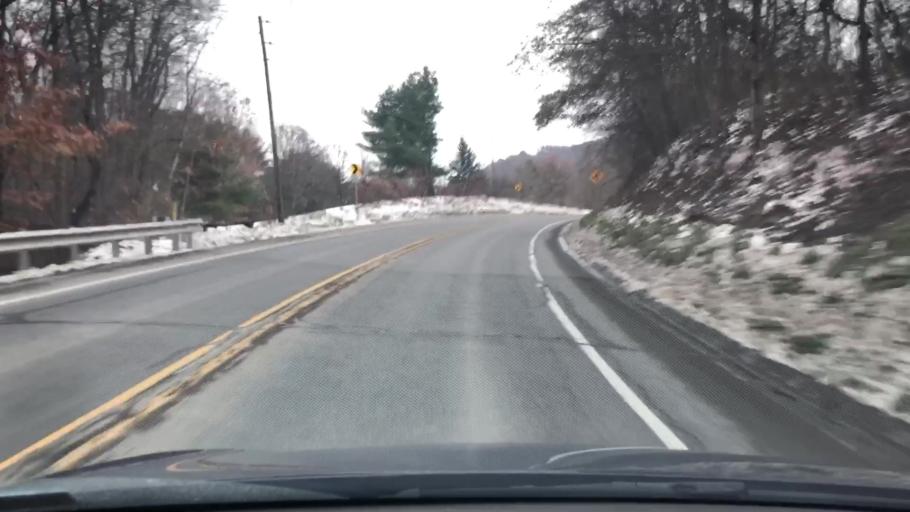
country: US
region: Pennsylvania
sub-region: Jefferson County
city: Brookville
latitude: 41.1283
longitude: -79.1627
